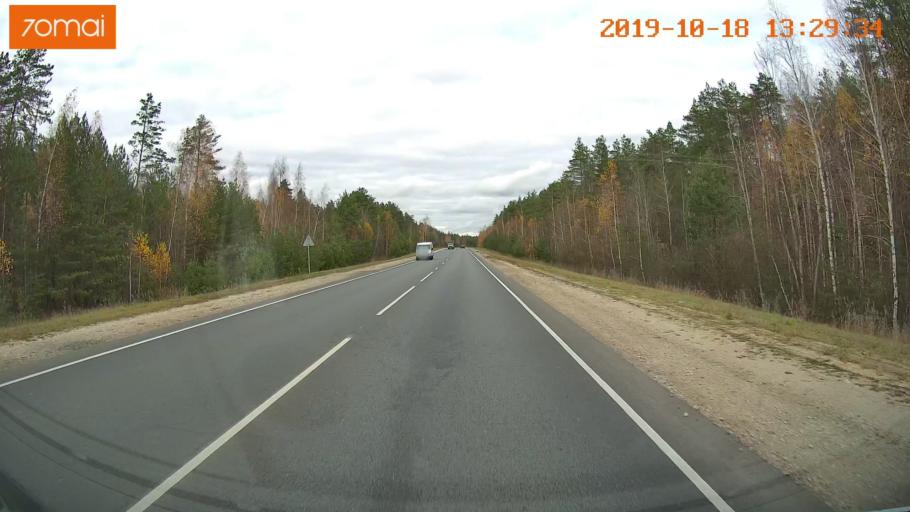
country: RU
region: Rjazan
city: Solotcha
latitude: 54.7965
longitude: 39.8757
